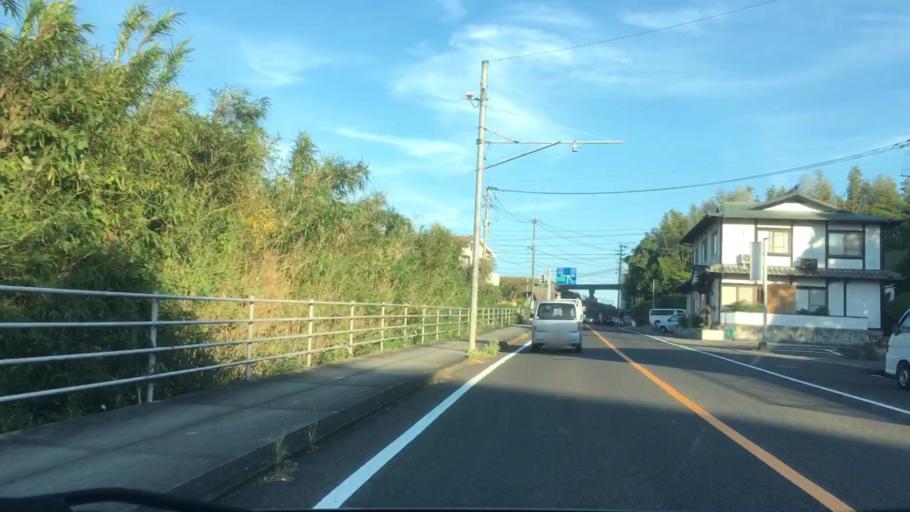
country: JP
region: Nagasaki
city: Sasebo
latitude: 33.0440
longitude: 129.7402
